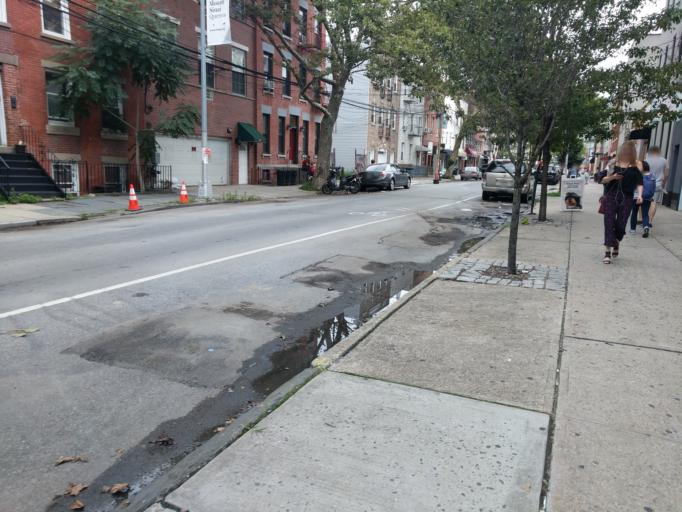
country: US
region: New York
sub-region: Queens County
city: Long Island City
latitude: 40.7432
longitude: -73.9562
